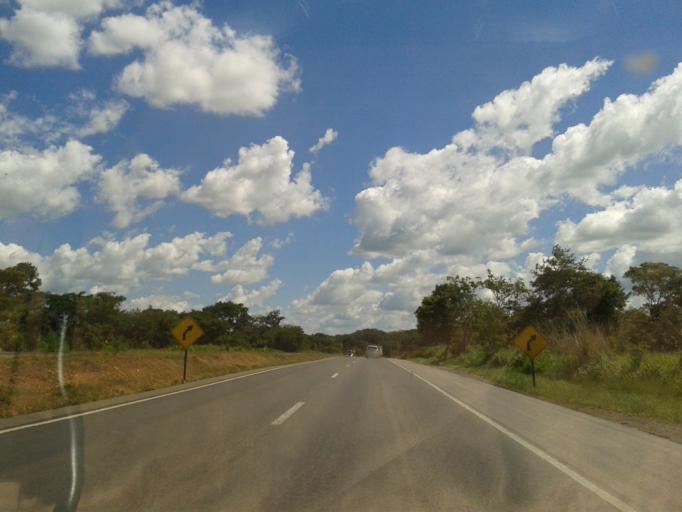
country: BR
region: Goias
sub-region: Piracanjuba
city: Piracanjuba
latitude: -17.3335
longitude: -49.2389
